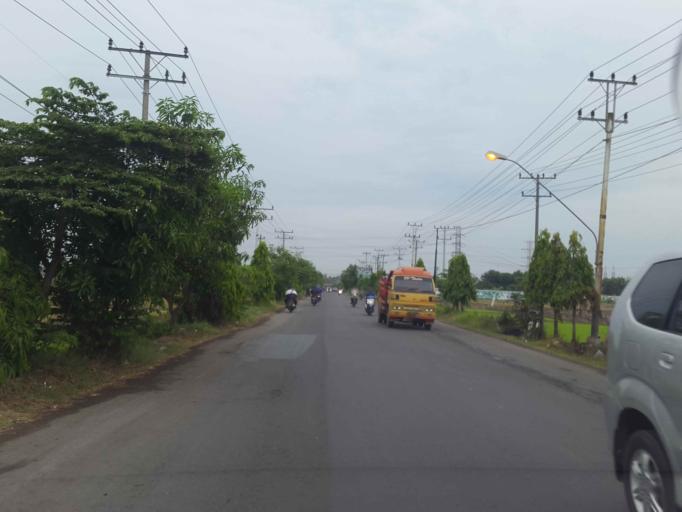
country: ID
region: Central Java
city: Adiwerna
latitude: -6.9169
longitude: 109.1264
